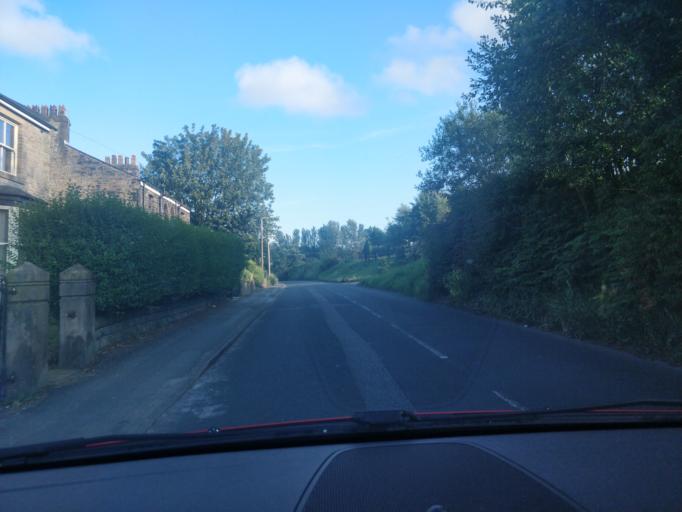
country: GB
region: England
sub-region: St. Helens
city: Billinge
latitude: 53.5367
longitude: -2.7211
